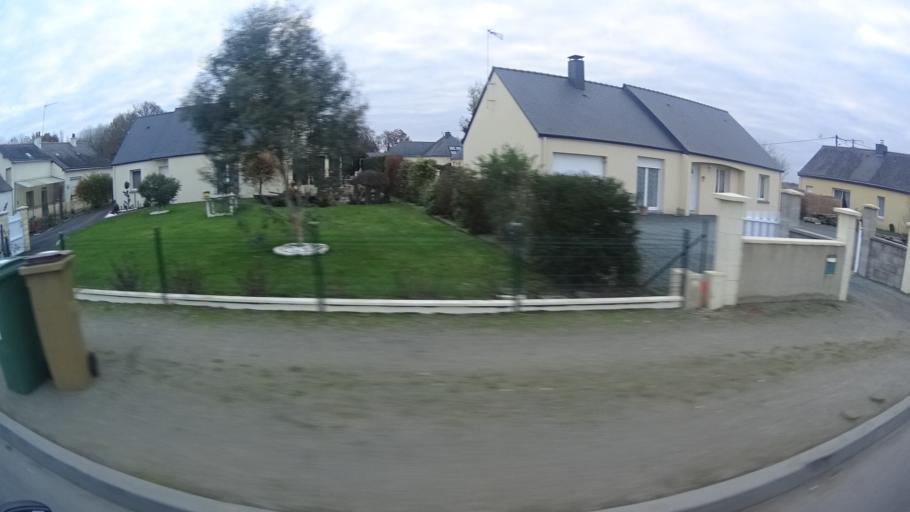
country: FR
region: Brittany
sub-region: Departement d'Ille-et-Vilaine
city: Langon
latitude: 47.6934
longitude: -1.8682
